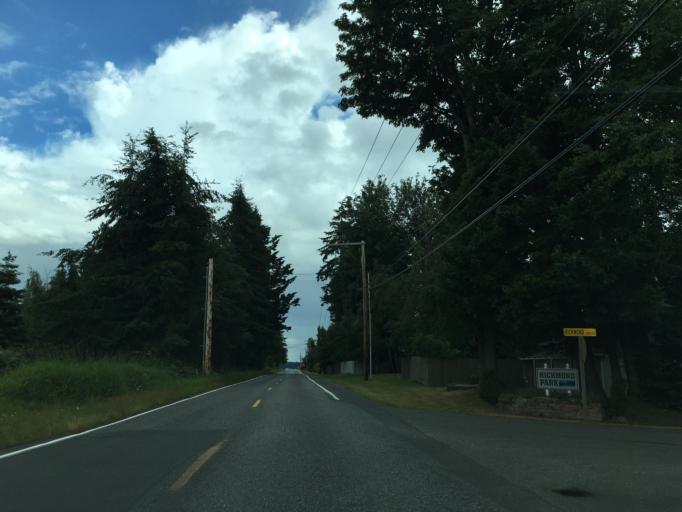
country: US
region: Washington
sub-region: Whatcom County
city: Birch Bay
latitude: 48.9461
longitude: -122.7648
